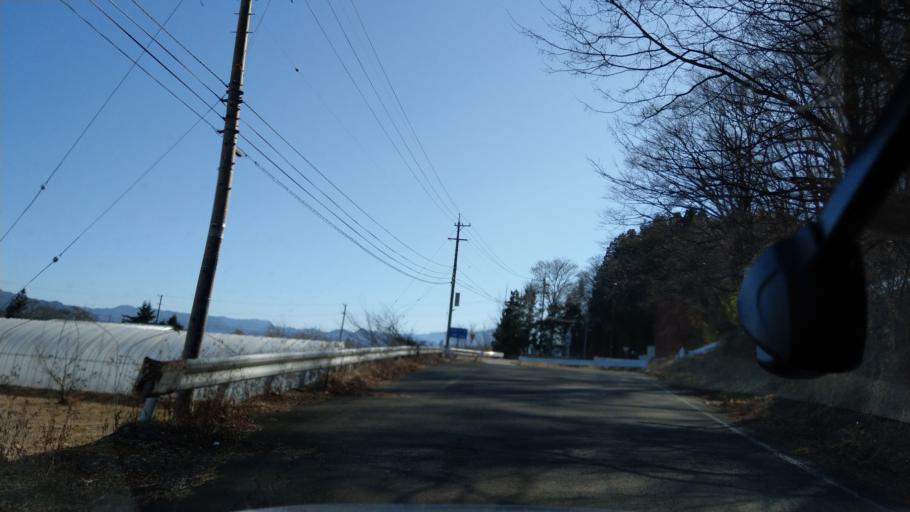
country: JP
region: Nagano
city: Saku
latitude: 36.2185
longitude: 138.4494
